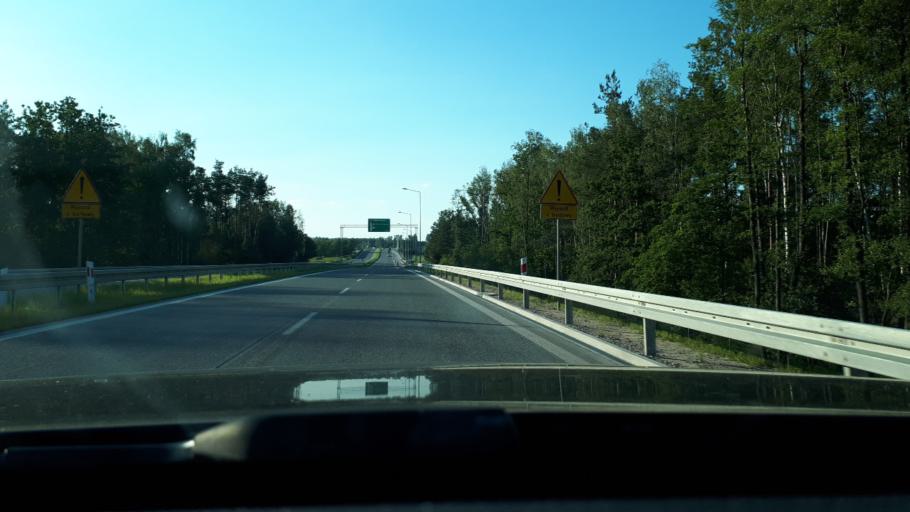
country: PL
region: Masovian Voivodeship
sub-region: Powiat piaseczynski
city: Baniocha
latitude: 51.9951
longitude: 21.1700
